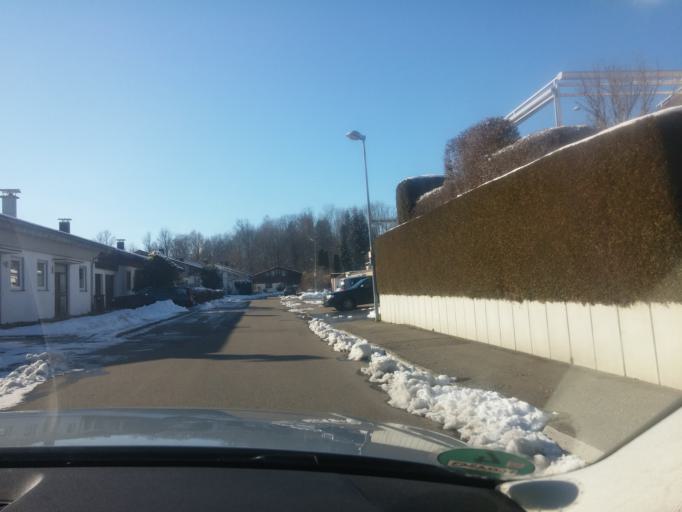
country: DE
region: Baden-Wuerttemberg
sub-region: Tuebingen Region
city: Leutkirch im Allgau
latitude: 47.8346
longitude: 10.0308
